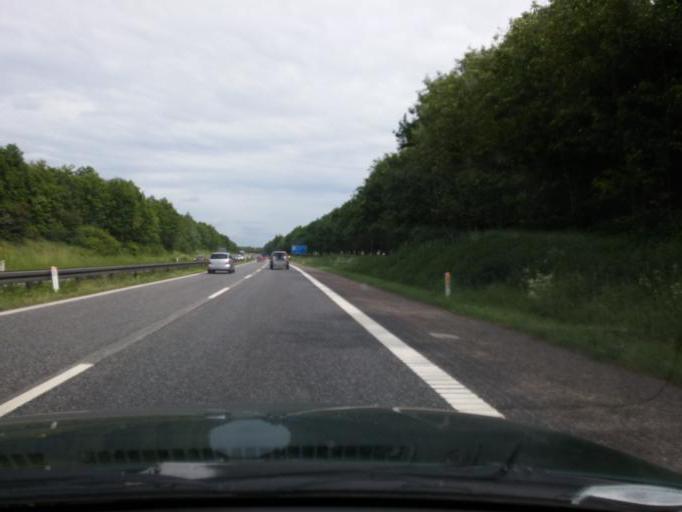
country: DK
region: South Denmark
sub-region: Odense Kommune
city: Bellinge
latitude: 55.3634
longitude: 10.3277
